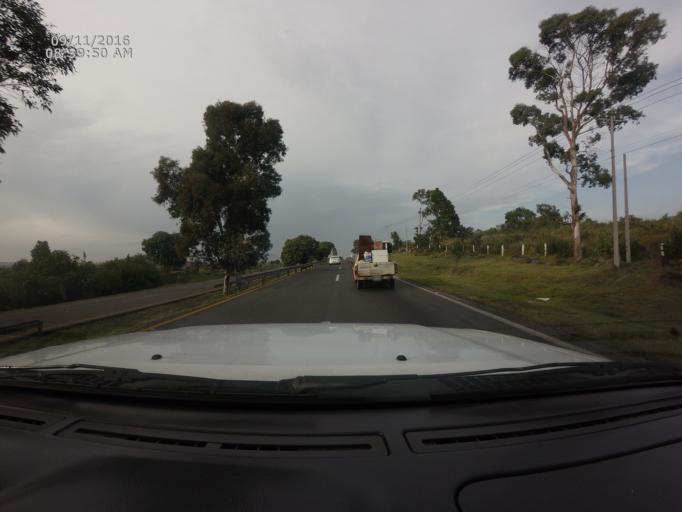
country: MX
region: Michoacan
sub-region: Morelia
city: La Mintzita (Piedra Dura)
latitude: 19.6168
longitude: -101.2828
